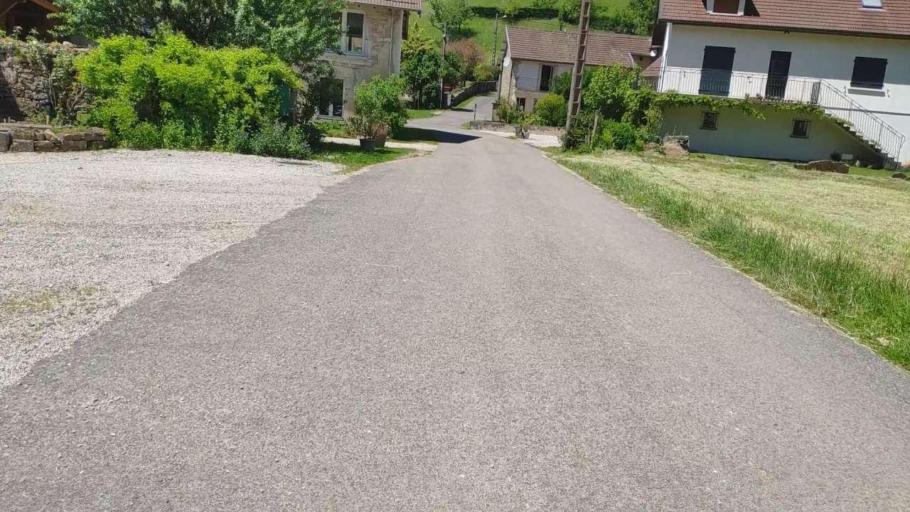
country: FR
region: Franche-Comte
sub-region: Departement du Jura
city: Poligny
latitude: 46.7497
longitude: 5.6713
